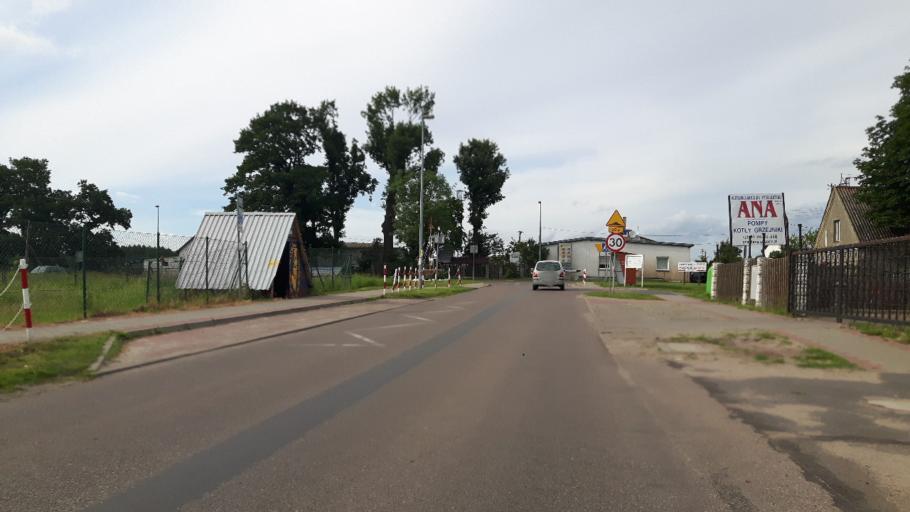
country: PL
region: West Pomeranian Voivodeship
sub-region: Powiat goleniowski
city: Goleniow
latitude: 53.4528
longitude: 14.7438
